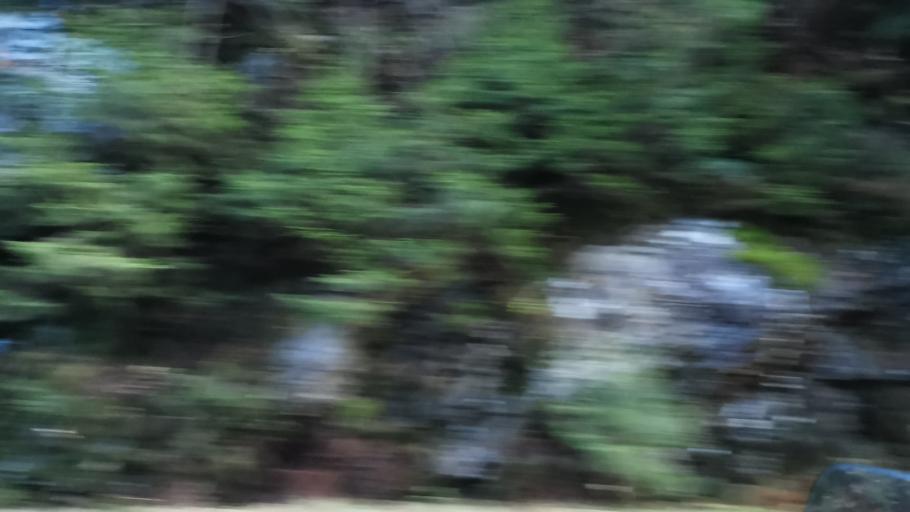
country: SE
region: Vaestra Goetaland
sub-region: Munkedals Kommun
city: Munkedal
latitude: 58.4082
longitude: 11.6728
